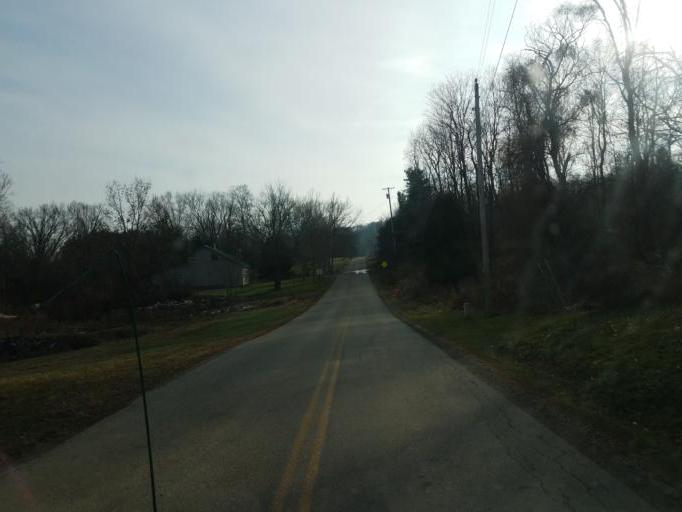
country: US
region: Ohio
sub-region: Richland County
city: Lincoln Heights
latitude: 40.7302
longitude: -82.3790
